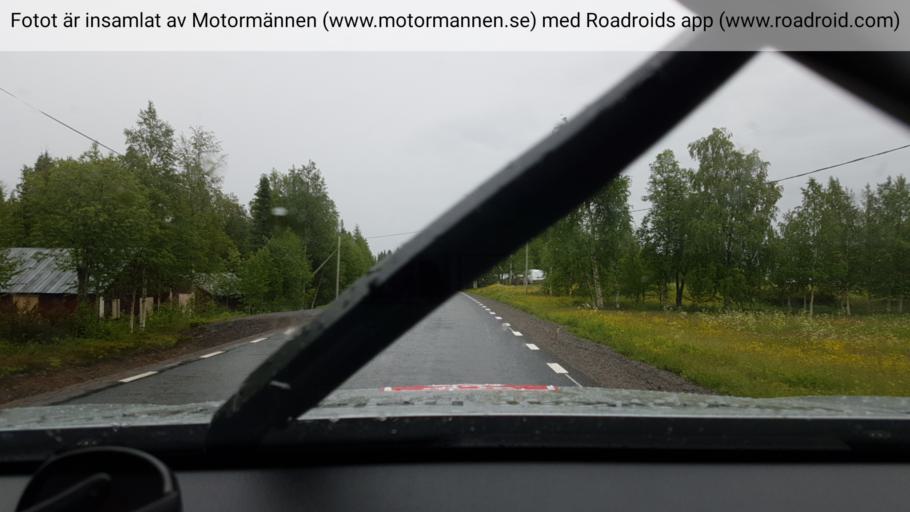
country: SE
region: Vaesterbotten
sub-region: Sorsele Kommun
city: Sorsele
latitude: 65.7994
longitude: 16.9626
